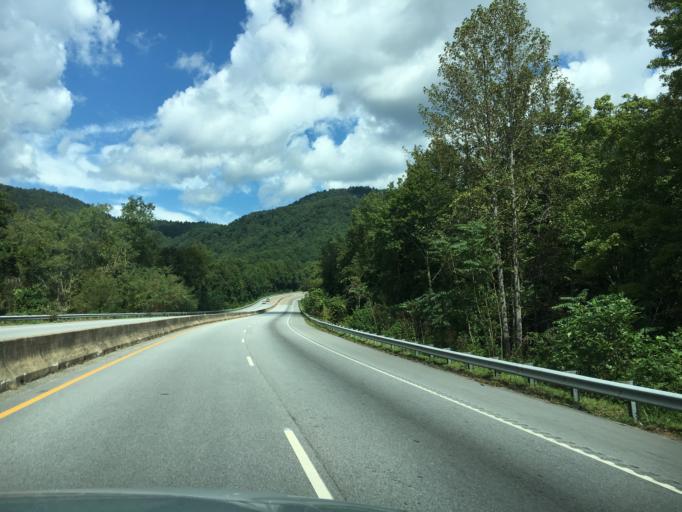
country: US
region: North Carolina
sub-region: Henderson County
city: Flat Rock
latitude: 35.1568
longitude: -82.4737
